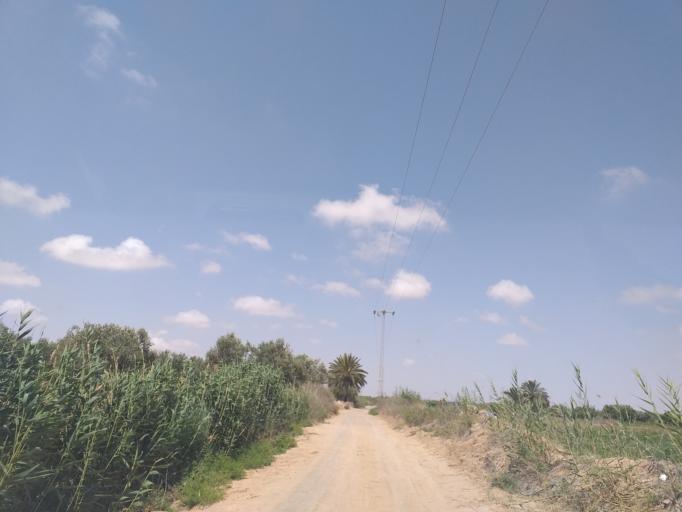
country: TN
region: Qabis
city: Gabes
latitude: 33.9527
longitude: 10.0451
